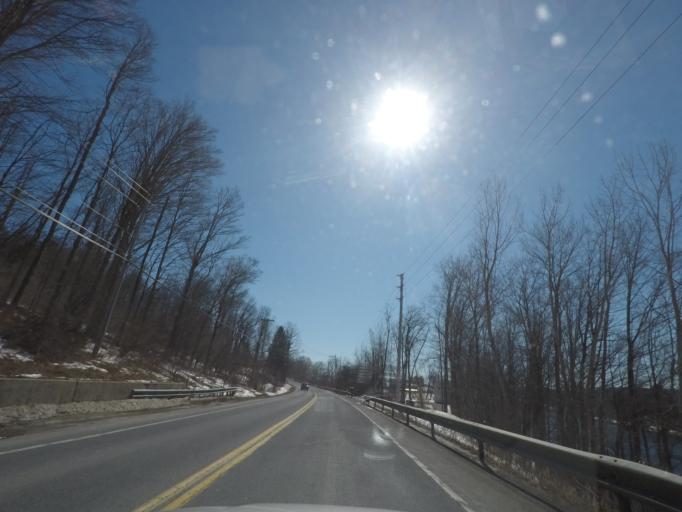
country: US
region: New York
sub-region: Saratoga County
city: Stillwater
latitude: 42.9282
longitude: -73.6431
